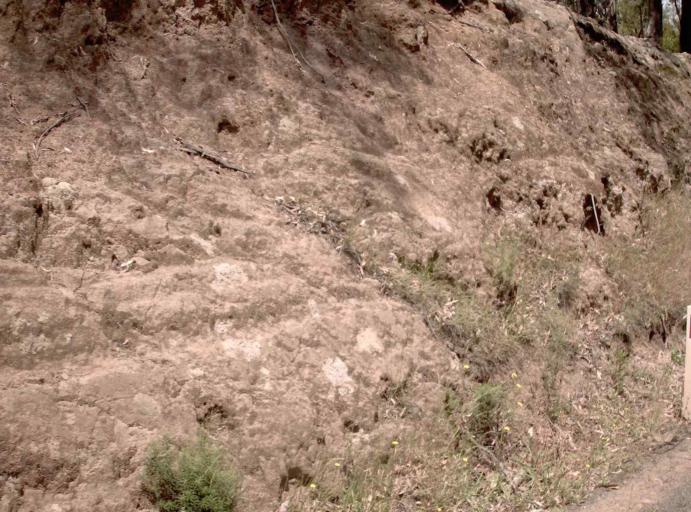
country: AU
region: Victoria
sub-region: Latrobe
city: Traralgon
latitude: -38.3824
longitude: 146.7582
